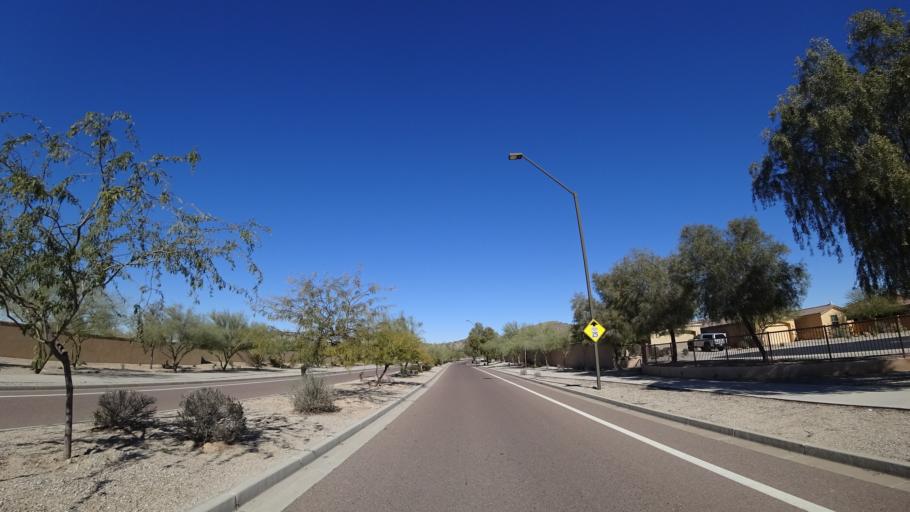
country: US
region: Arizona
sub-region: Maricopa County
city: Goodyear
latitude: 33.3317
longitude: -112.4478
